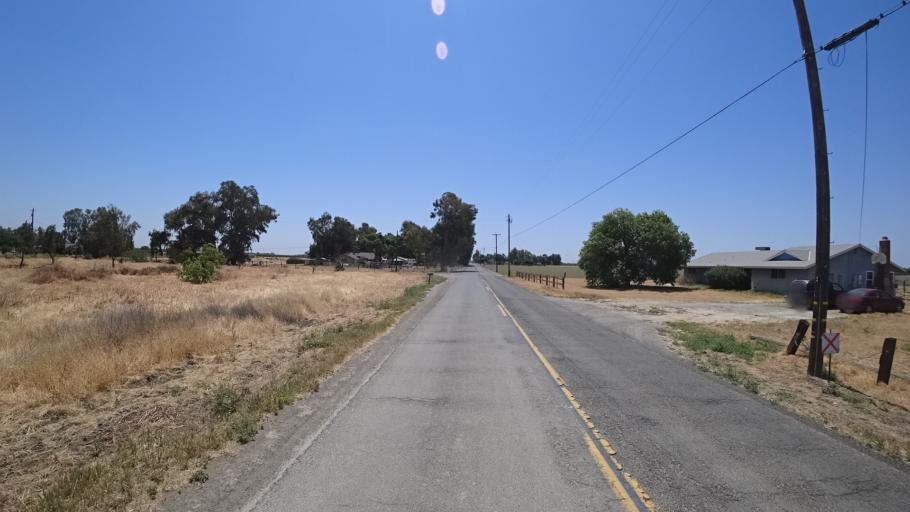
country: US
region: California
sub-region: Kings County
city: Lemoore
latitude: 36.2753
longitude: -119.7629
